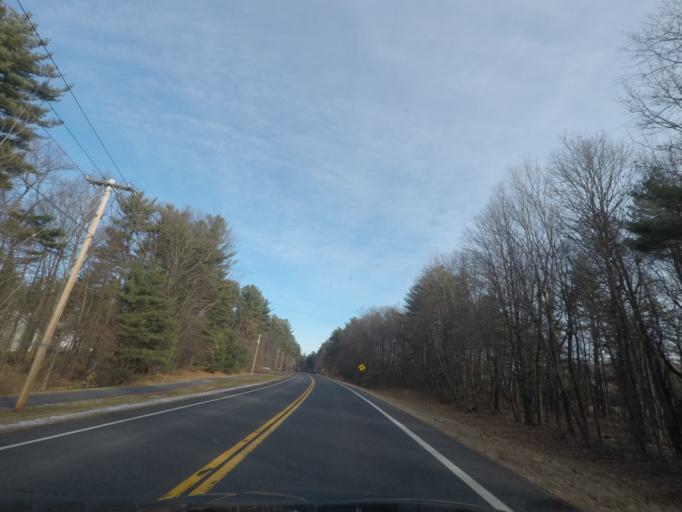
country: US
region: New York
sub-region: Saratoga County
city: Country Knolls
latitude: 42.9780
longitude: -73.7686
